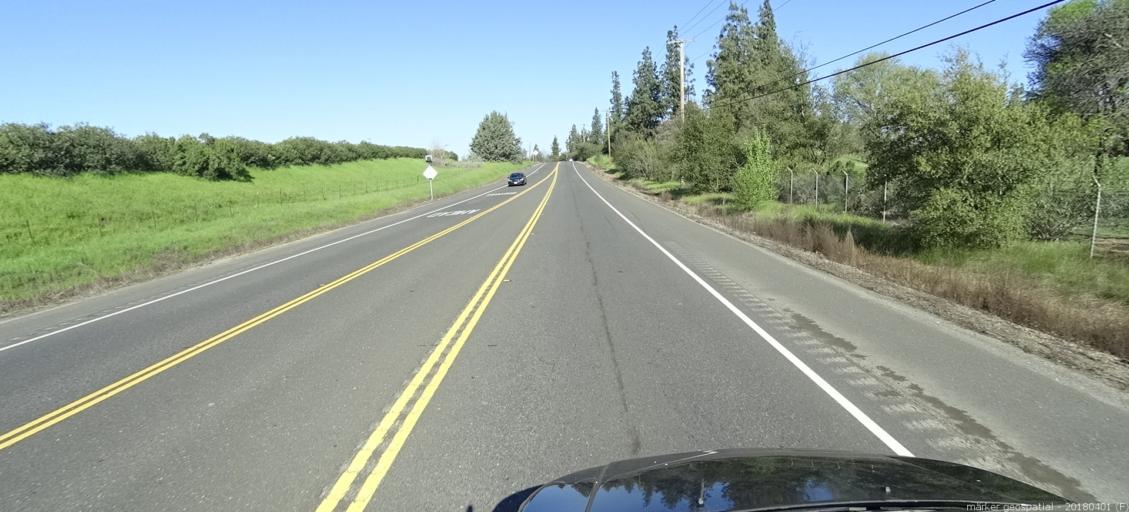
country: US
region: California
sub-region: Sacramento County
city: Rancho Murieta
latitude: 38.4886
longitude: -121.0843
